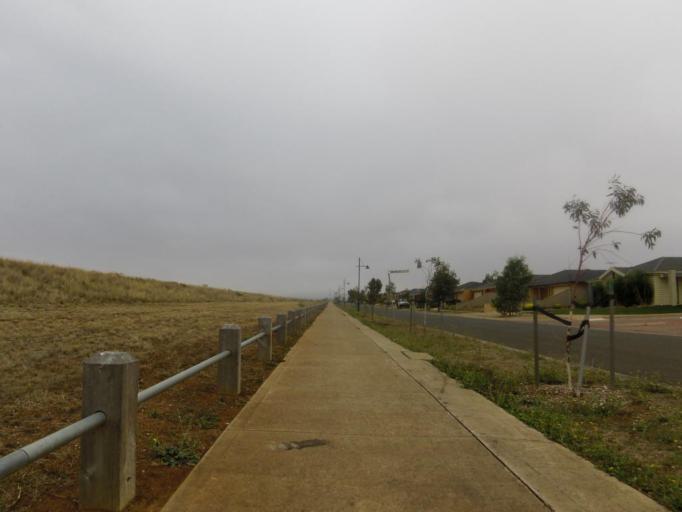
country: AU
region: Victoria
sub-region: Melton
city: Kurunjang
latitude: -37.6570
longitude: 144.5877
